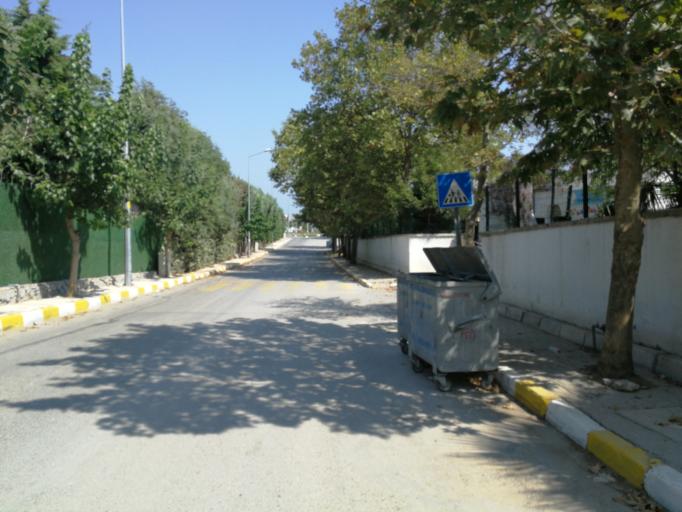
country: TR
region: Izmir
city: Urla
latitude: 38.3253
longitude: 26.7721
